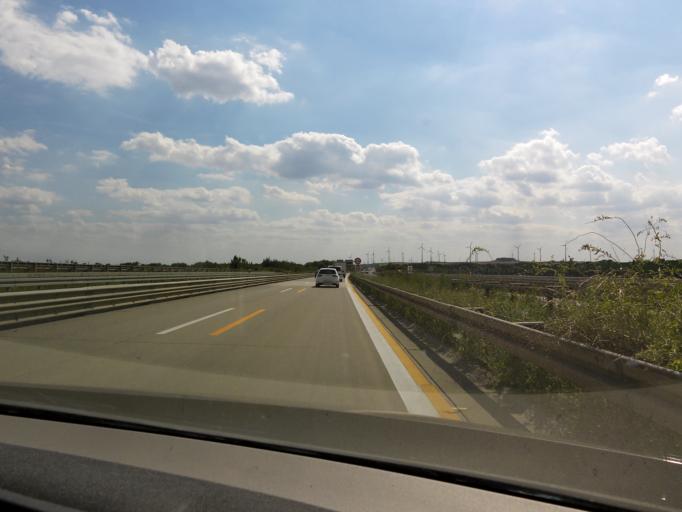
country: DE
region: Saxony-Anhalt
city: Ilberstedt
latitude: 51.8016
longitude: 11.6835
